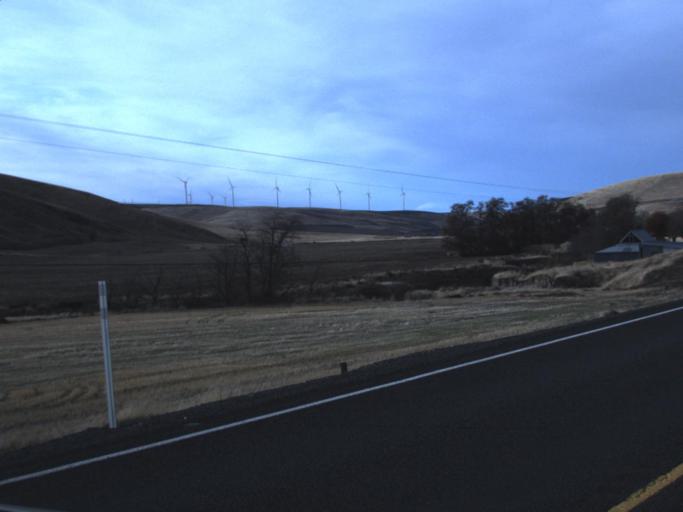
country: US
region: Washington
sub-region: Garfield County
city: Pomeroy
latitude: 46.5153
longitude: -117.7900
